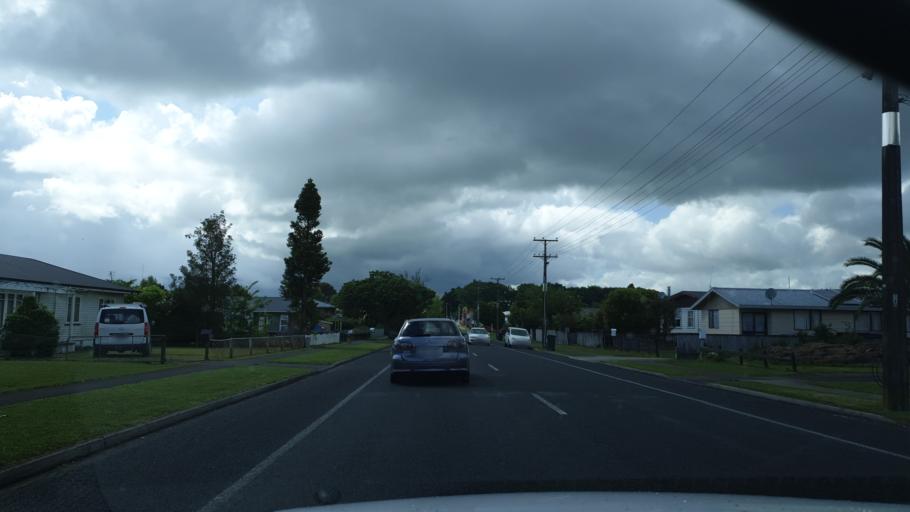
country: NZ
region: Waikato
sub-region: Matamata-Piako District
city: Matamata
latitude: -37.8072
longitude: 175.7670
